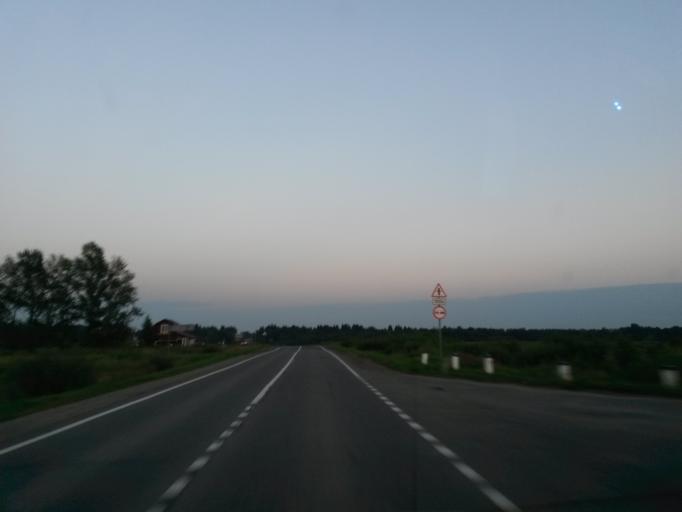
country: RU
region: Jaroslavl
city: Yaroslavl
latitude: 57.7902
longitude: 39.8316
